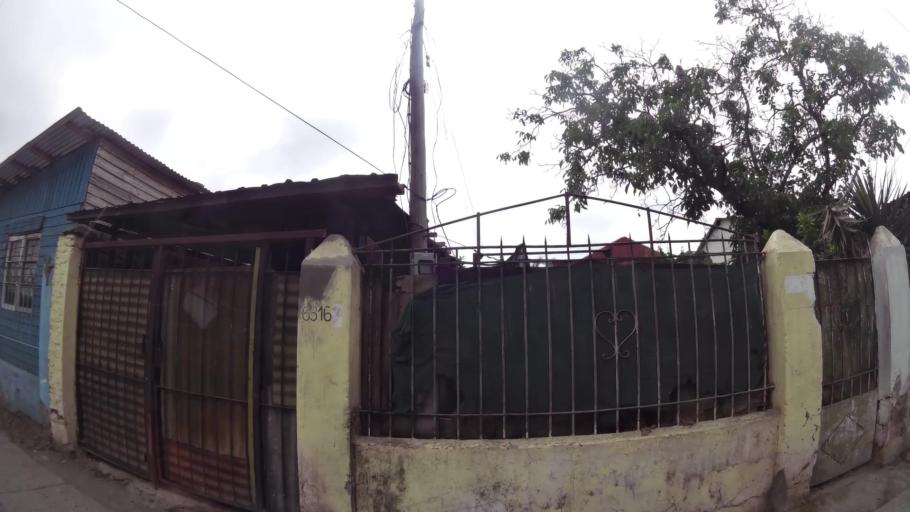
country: CL
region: Santiago Metropolitan
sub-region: Provincia de Santiago
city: Santiago
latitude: -33.5031
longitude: -70.6882
